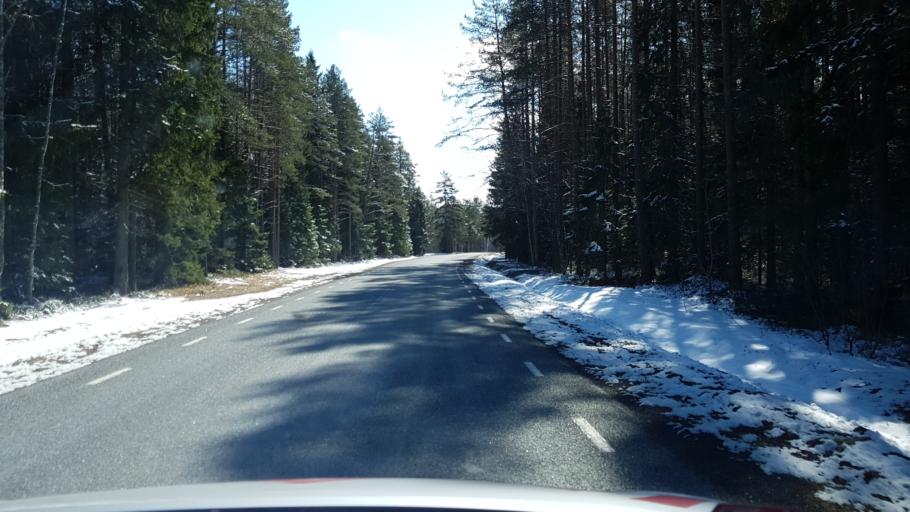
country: EE
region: Laeaene-Virumaa
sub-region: Kadrina vald
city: Kadrina
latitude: 59.4882
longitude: 25.9894
